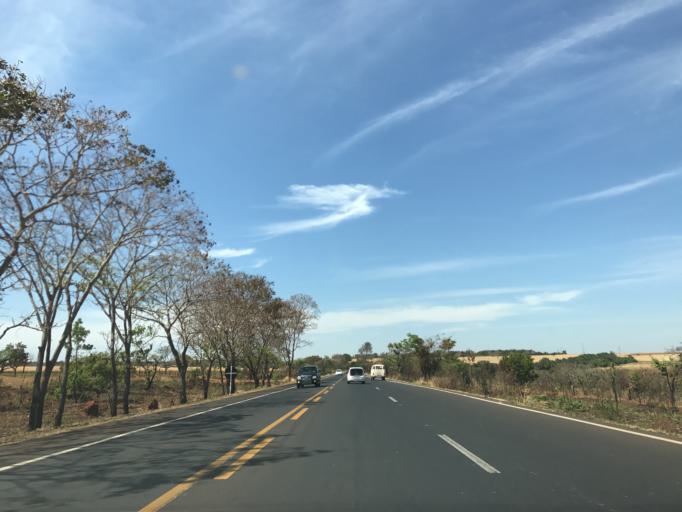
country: BR
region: Minas Gerais
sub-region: Monte Alegre De Minas
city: Monte Alegre de Minas
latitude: -18.9595
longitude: -49.0284
